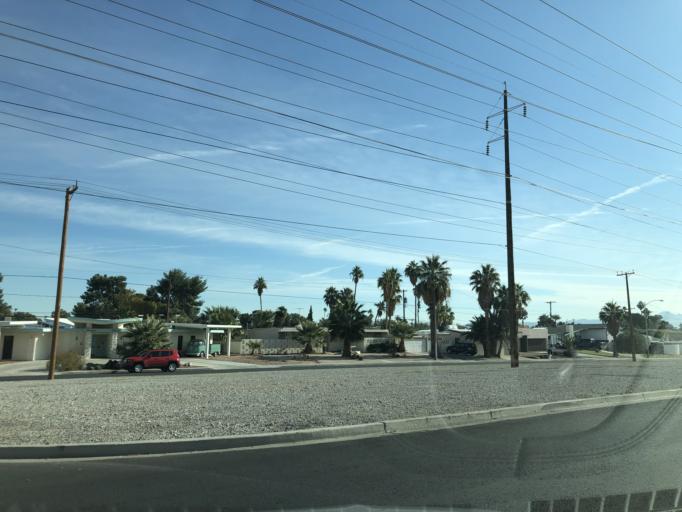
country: US
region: Nevada
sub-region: Clark County
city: Winchester
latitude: 36.1245
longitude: -115.1282
